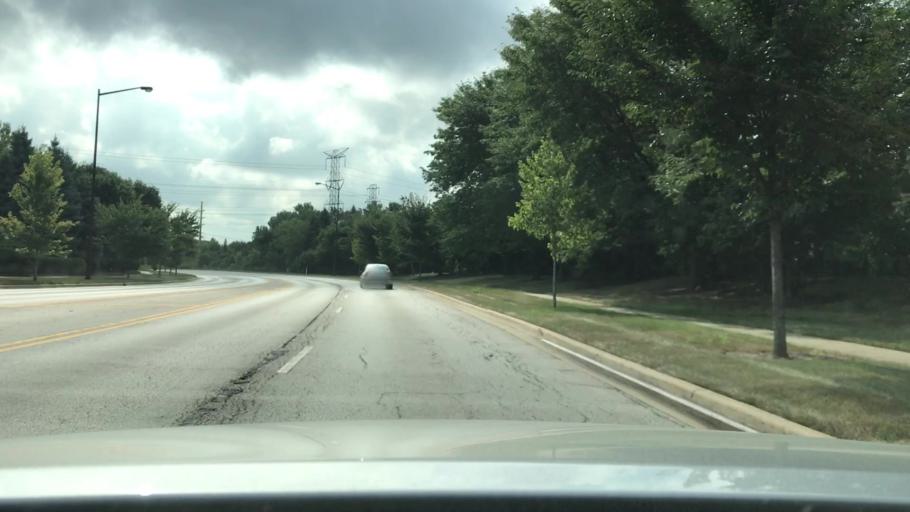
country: US
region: Illinois
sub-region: Kane County
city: Aurora
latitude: 41.7549
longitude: -88.2364
